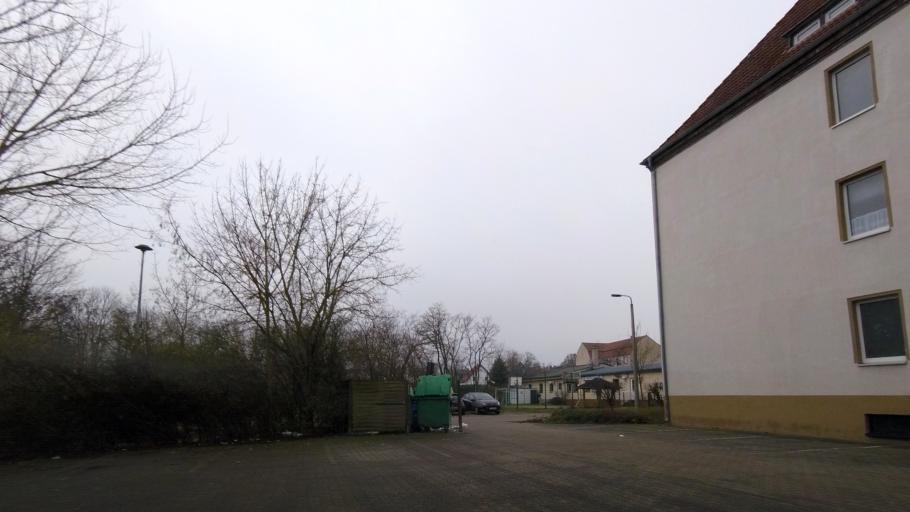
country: DE
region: Brandenburg
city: Juterbog
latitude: 51.9989
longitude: 13.0543
